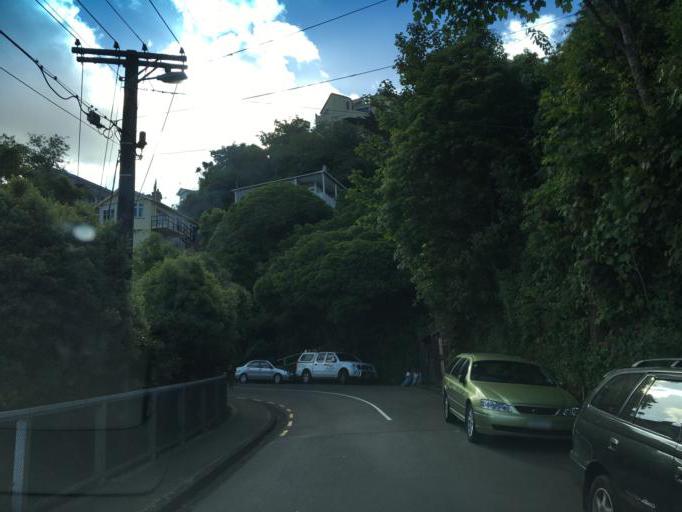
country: NZ
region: Wellington
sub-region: Wellington City
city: Kelburn
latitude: -41.2832
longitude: 174.7610
